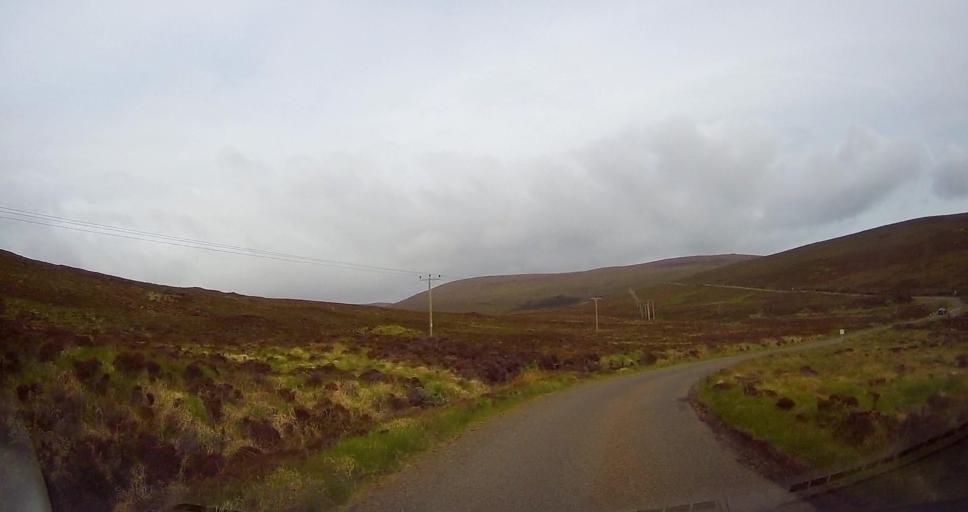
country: GB
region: Scotland
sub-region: Orkney Islands
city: Stromness
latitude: 58.8687
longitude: -3.2309
